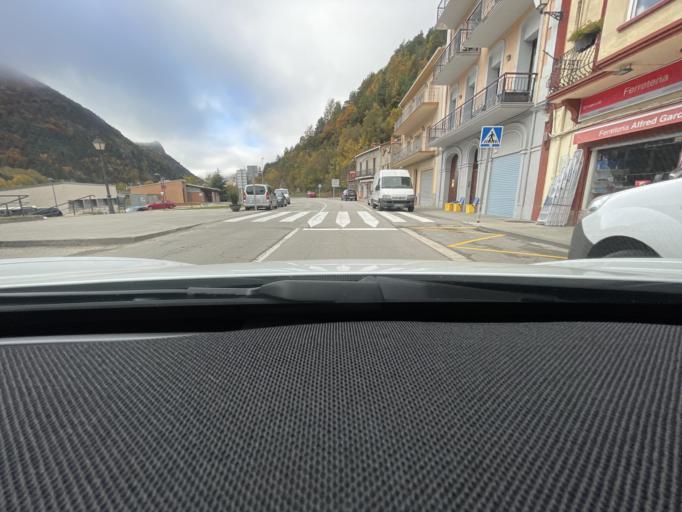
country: ES
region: Catalonia
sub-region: Provincia de Barcelona
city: Guardiola de Bergueda
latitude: 42.2305
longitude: 1.8774
